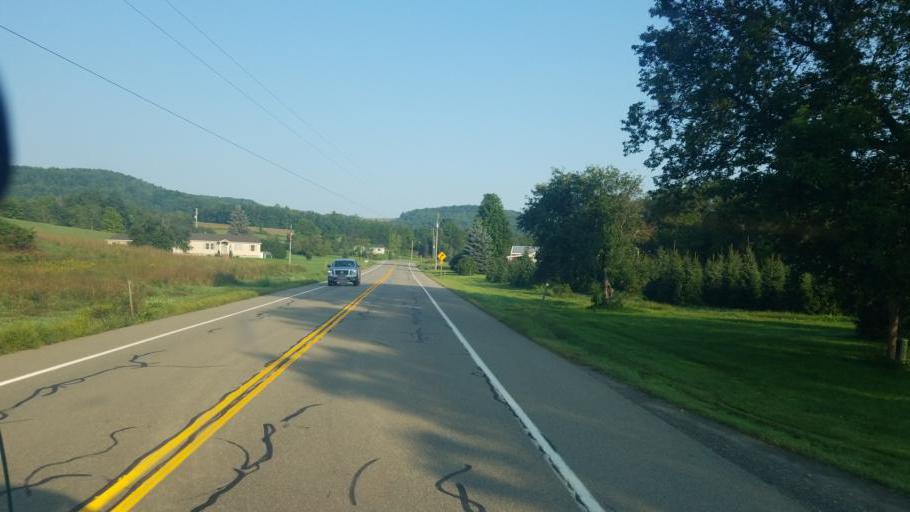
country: US
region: Pennsylvania
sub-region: Tioga County
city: Westfield
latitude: 42.0079
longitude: -77.5139
